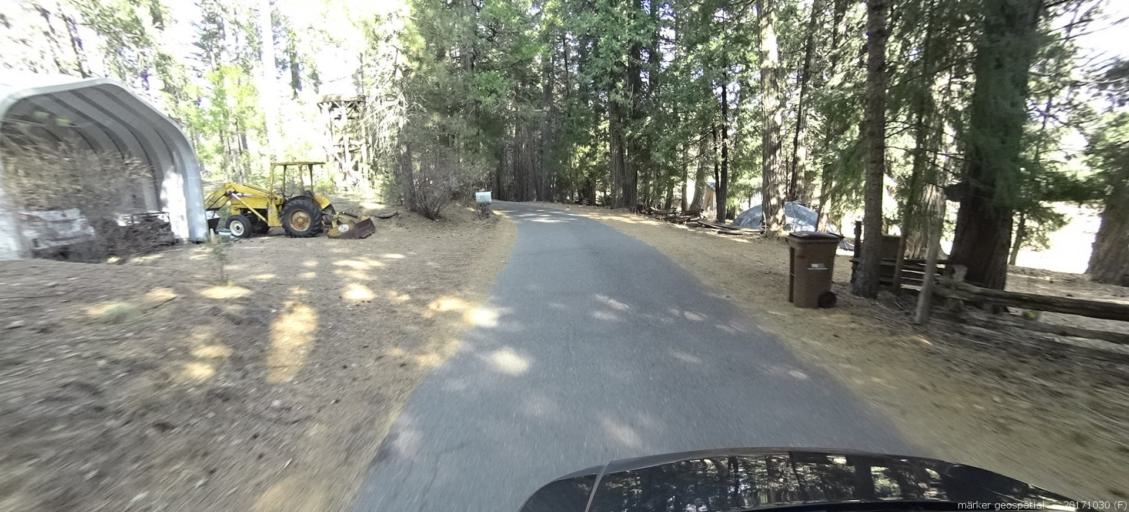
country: US
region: California
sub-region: Shasta County
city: Shingletown
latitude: 40.5066
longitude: -121.7388
